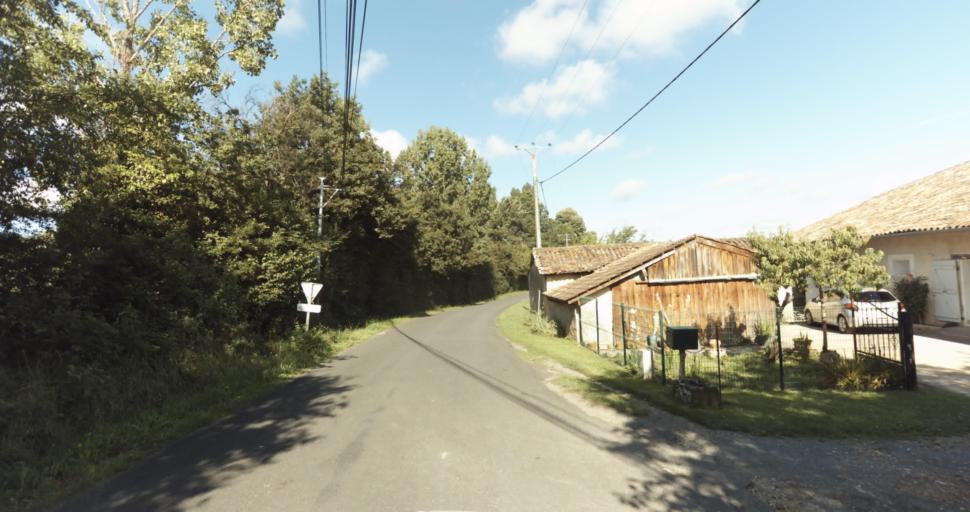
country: FR
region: Aquitaine
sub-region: Departement de la Gironde
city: Bazas
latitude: 44.4251
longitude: -0.2074
